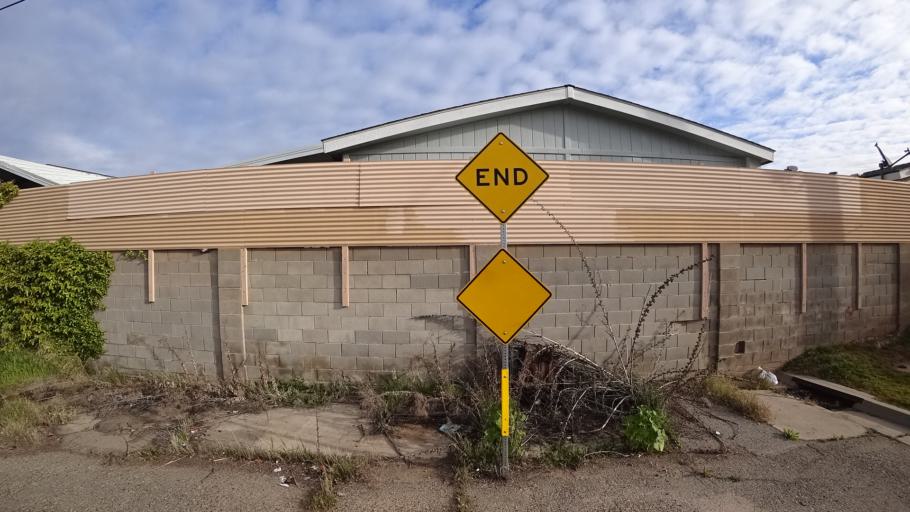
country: US
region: California
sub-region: Fresno County
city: Fresno
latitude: 36.8337
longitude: -119.7943
